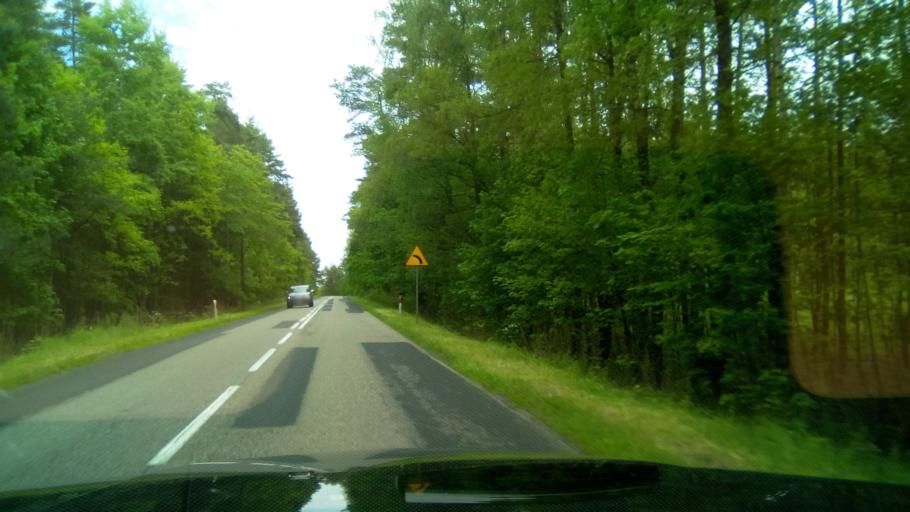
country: PL
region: Pomeranian Voivodeship
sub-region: Powiat bytowski
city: Czarna Dabrowka
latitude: 54.3395
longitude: 17.5485
